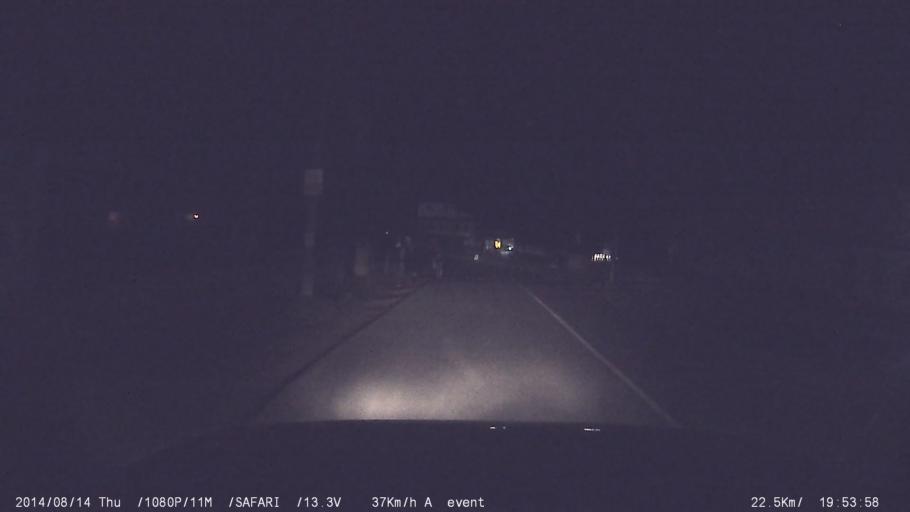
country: IN
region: Kerala
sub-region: Kottayam
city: Kottayam
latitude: 9.6563
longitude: 76.5511
